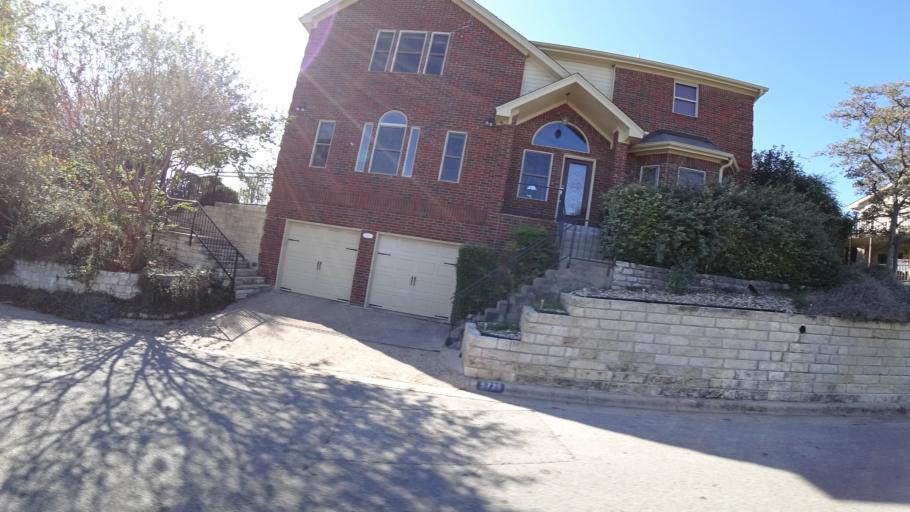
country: US
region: Texas
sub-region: Williamson County
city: Jollyville
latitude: 30.4034
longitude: -97.7620
